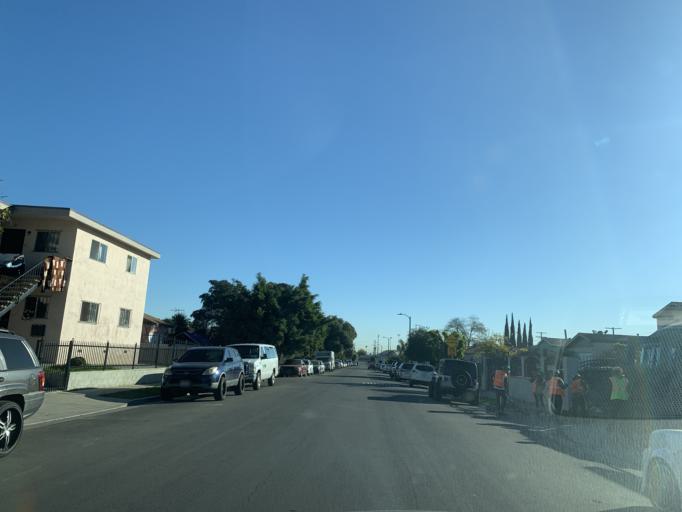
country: US
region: California
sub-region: Los Angeles County
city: Westmont
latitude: 33.9320
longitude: -118.2782
